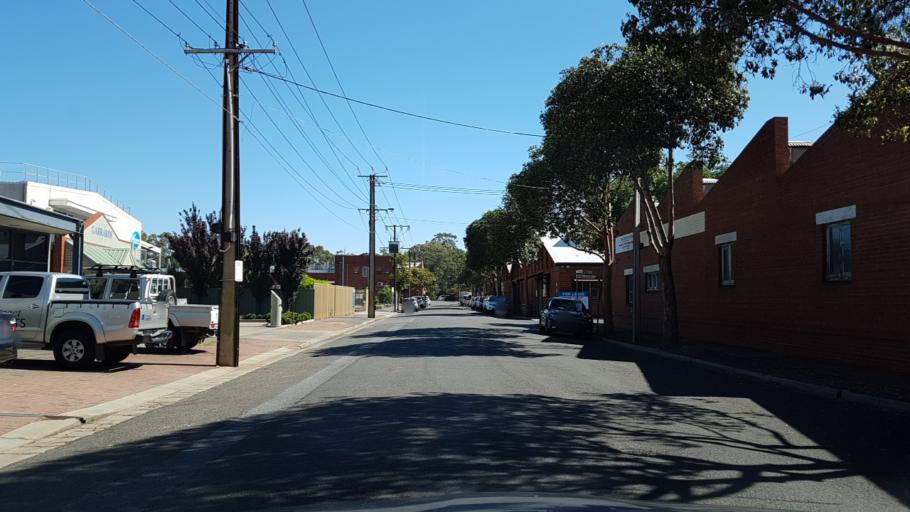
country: AU
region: South Australia
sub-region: City of West Torrens
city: Thebarton
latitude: -34.9125
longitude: 138.5725
